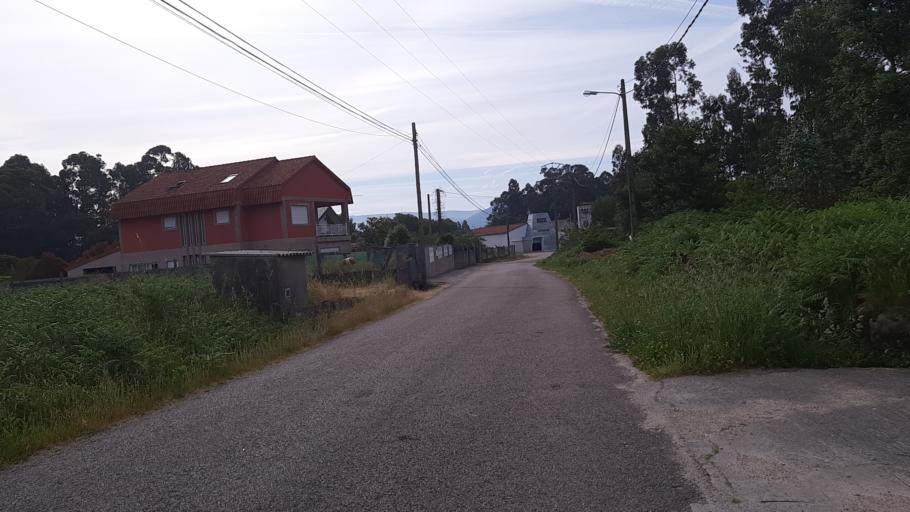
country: ES
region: Galicia
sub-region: Provincia de Pontevedra
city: O Rosal
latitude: 41.9275
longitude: -8.8427
